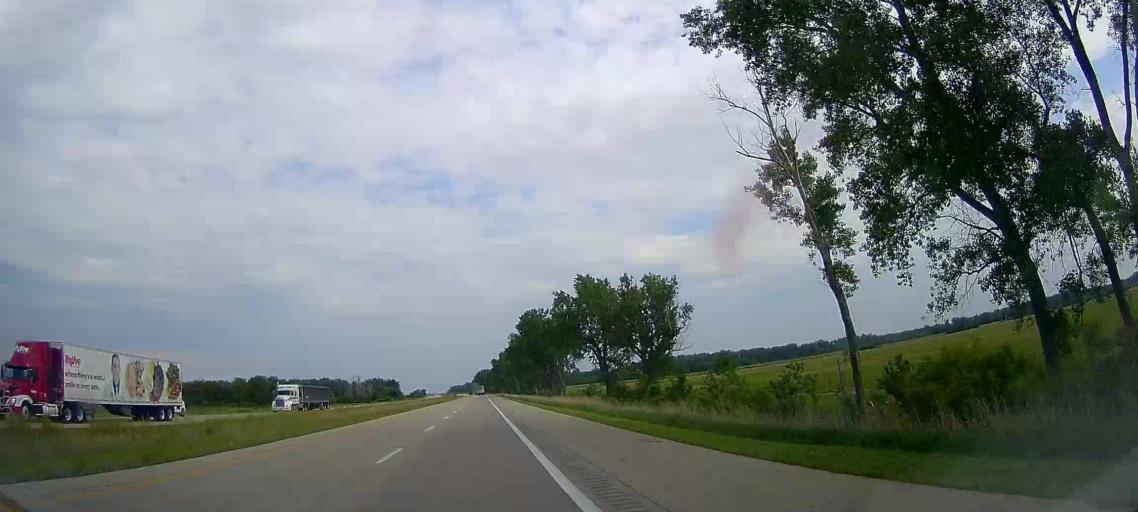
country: US
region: Nebraska
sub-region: Burt County
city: Tekamah
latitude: 41.8261
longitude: -96.0773
